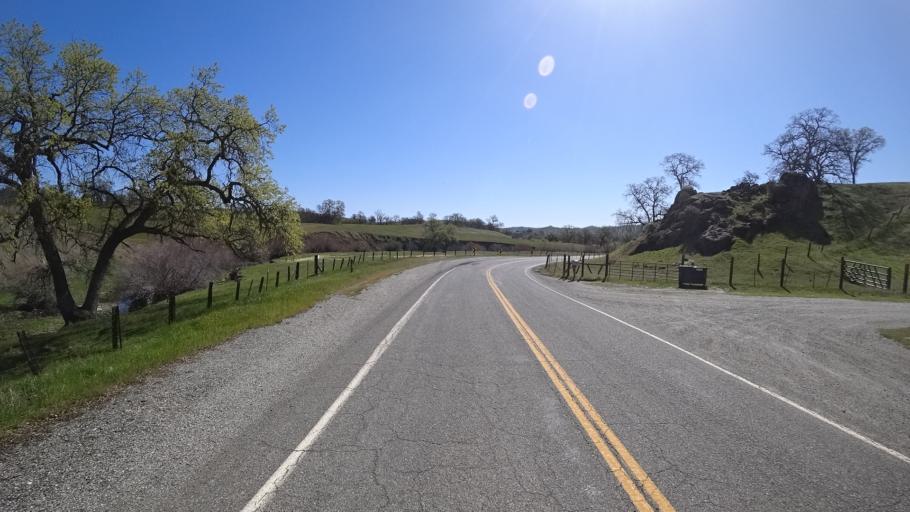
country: US
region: California
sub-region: Glenn County
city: Orland
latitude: 39.6827
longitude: -122.5360
